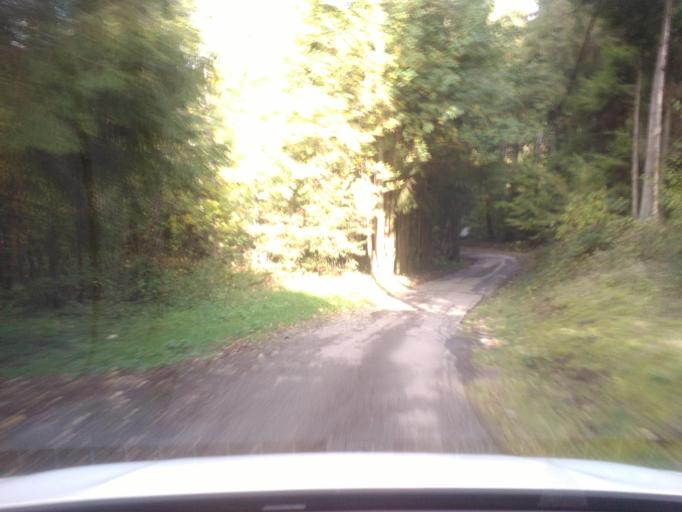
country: FR
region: Lorraine
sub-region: Departement des Vosges
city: Senones
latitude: 48.4077
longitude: 7.0711
